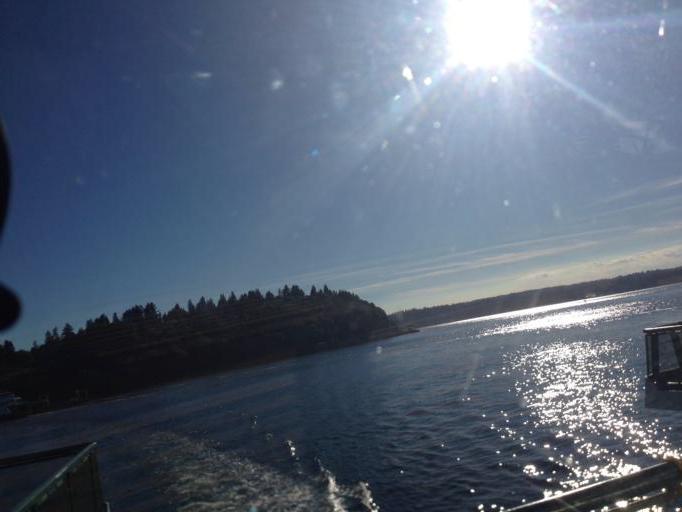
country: US
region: Washington
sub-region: Kitsap County
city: Southworth
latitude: 47.5146
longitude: -122.4607
